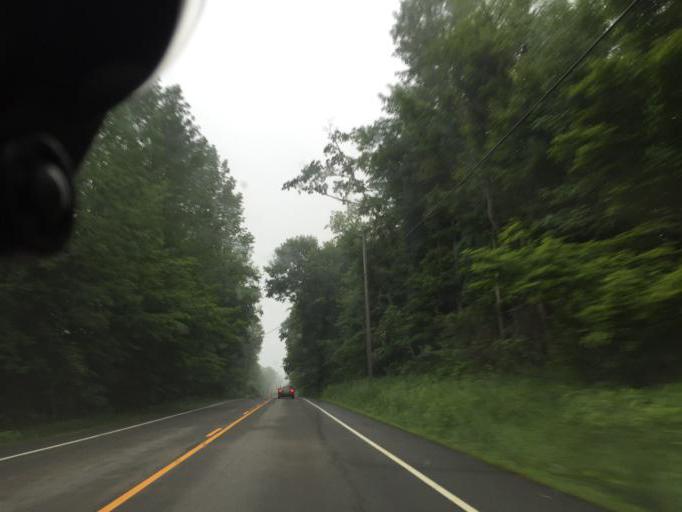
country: US
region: Connecticut
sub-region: Litchfield County
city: Winchester Center
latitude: 41.8729
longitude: -73.2494
